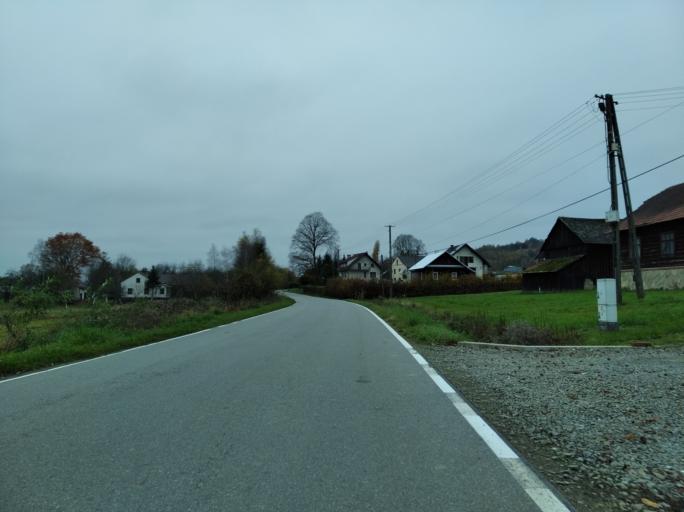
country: PL
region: Subcarpathian Voivodeship
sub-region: Powiat krosnienski
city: Leki
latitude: 49.8169
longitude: 21.6512
